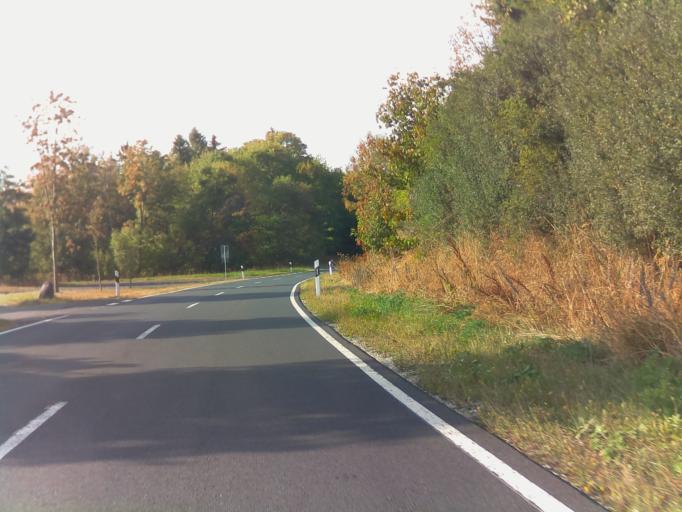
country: DE
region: Thuringia
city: Birx
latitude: 50.5130
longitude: 10.0368
